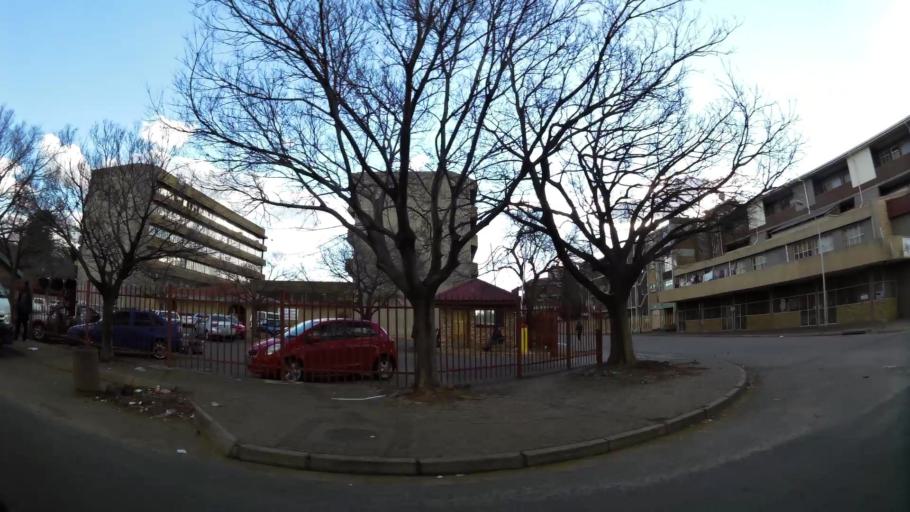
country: ZA
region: North-West
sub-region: Dr Kenneth Kaunda District Municipality
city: Potchefstroom
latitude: -26.7119
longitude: 27.0962
